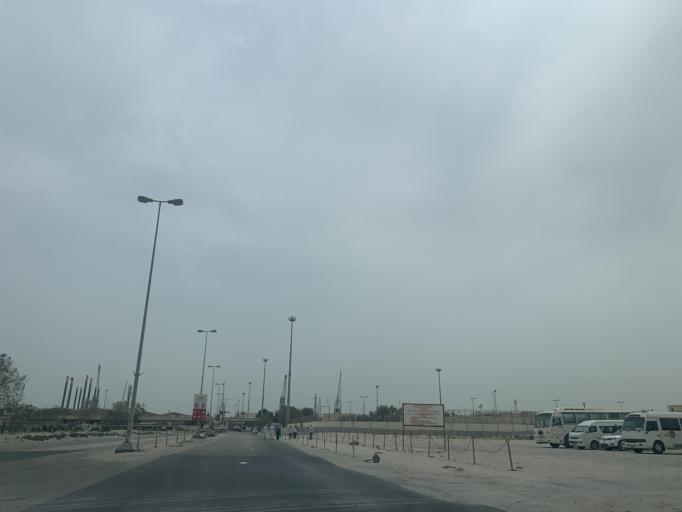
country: BH
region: Muharraq
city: Al Hadd
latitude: 26.1953
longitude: 50.6639
